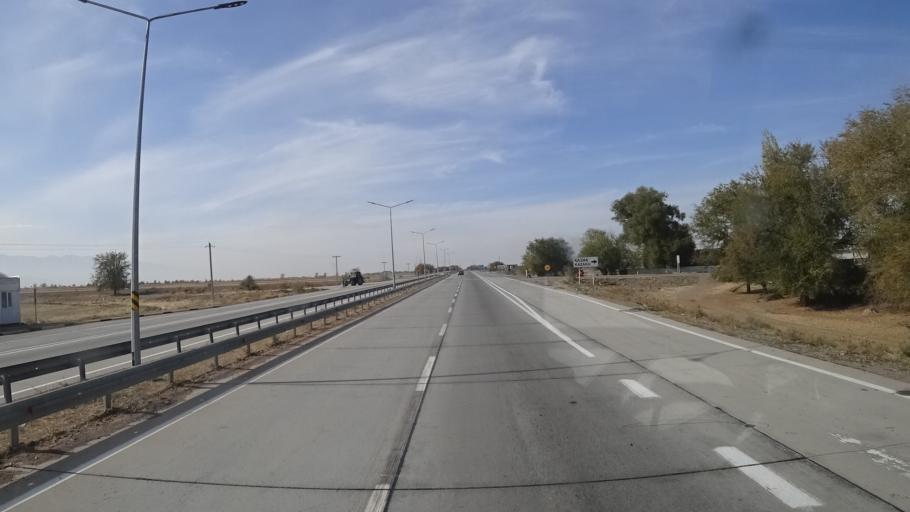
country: KZ
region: Zhambyl
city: Lugovoy
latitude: 42.9055
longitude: 72.9128
